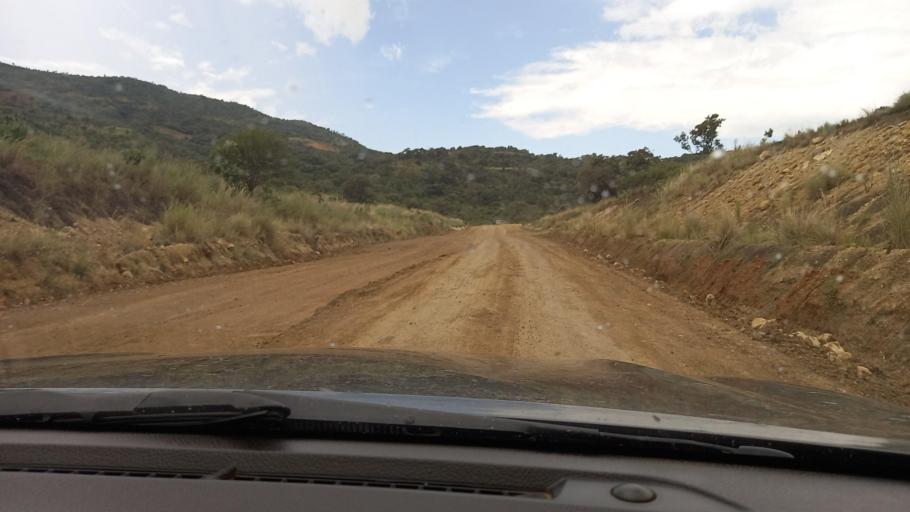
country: ET
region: Southern Nations, Nationalities, and People's Region
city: Mizan Teferi
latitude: 6.1966
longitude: 35.6734
